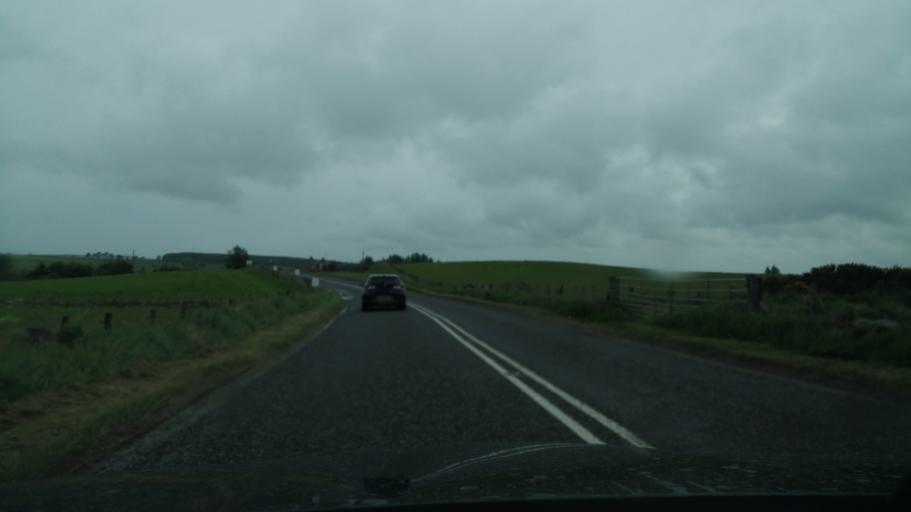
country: GB
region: Scotland
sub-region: Aberdeenshire
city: Portsoy
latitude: 57.5902
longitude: -2.7369
